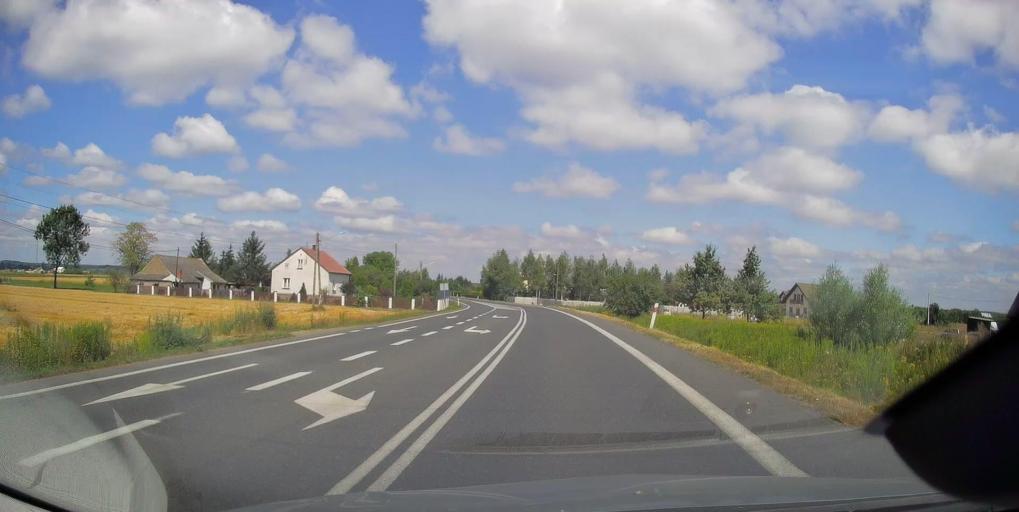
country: PL
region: Subcarpathian Voivodeship
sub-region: Powiat debicki
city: Brzeznica
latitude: 50.1469
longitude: 21.4862
